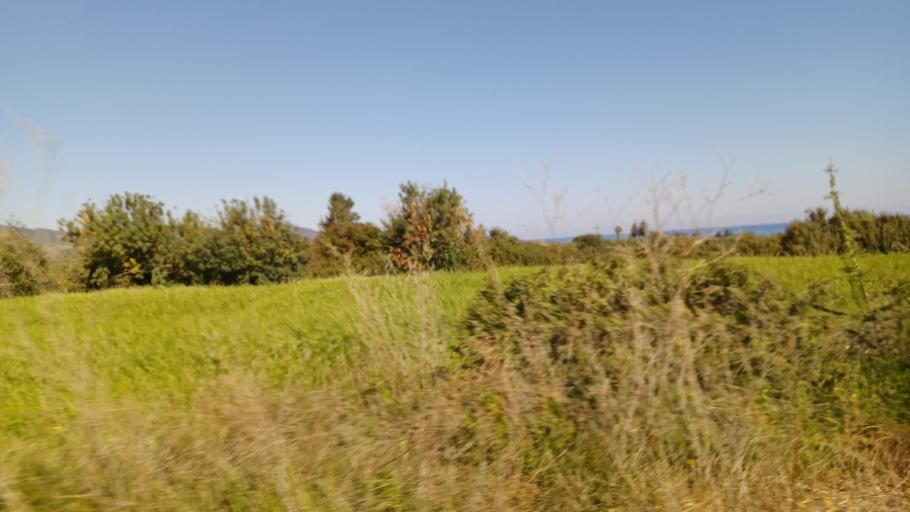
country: CY
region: Pafos
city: Polis
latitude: 35.0313
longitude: 32.3939
